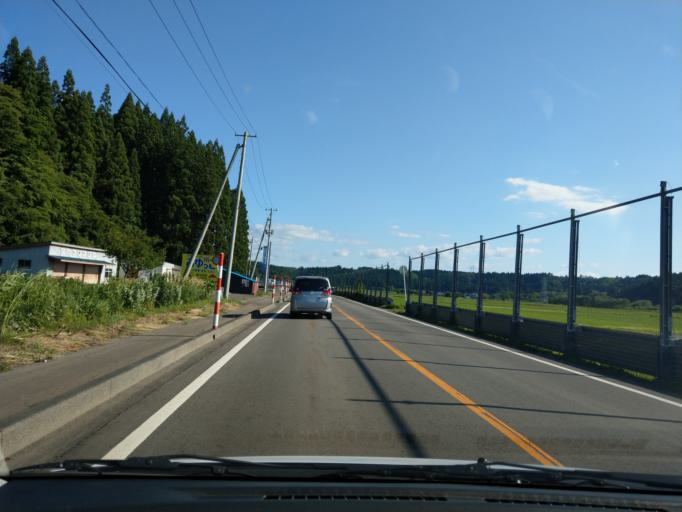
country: JP
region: Akita
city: Takanosu
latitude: 40.1845
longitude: 140.4003
